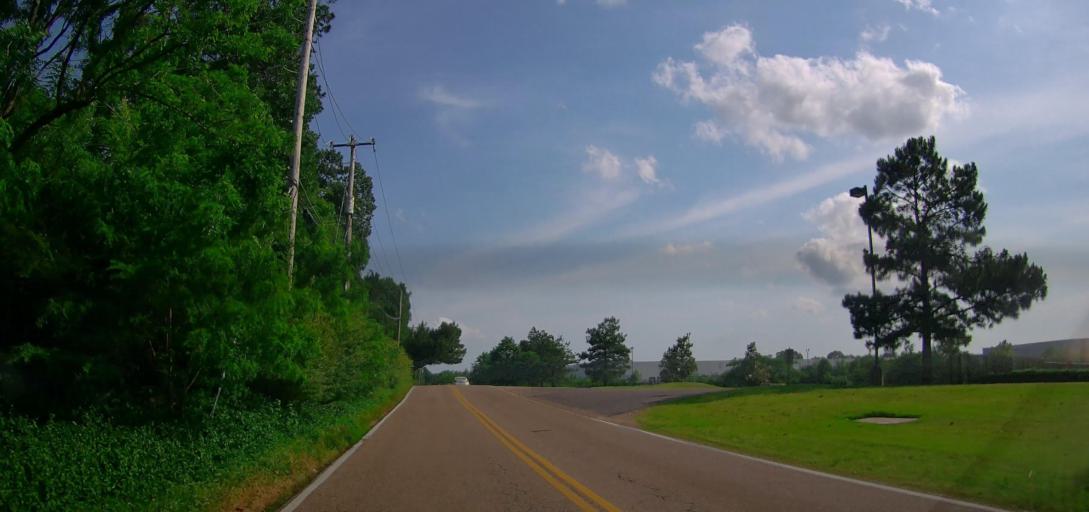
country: US
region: Mississippi
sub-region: De Soto County
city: Olive Branch
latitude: 35.0105
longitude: -89.8486
